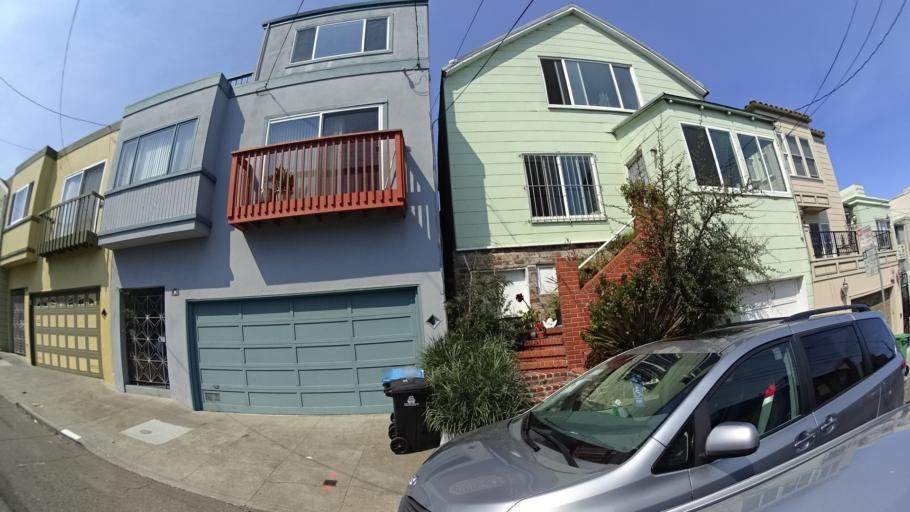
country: US
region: California
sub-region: San Mateo County
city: Daly City
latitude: 37.7205
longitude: -122.4519
